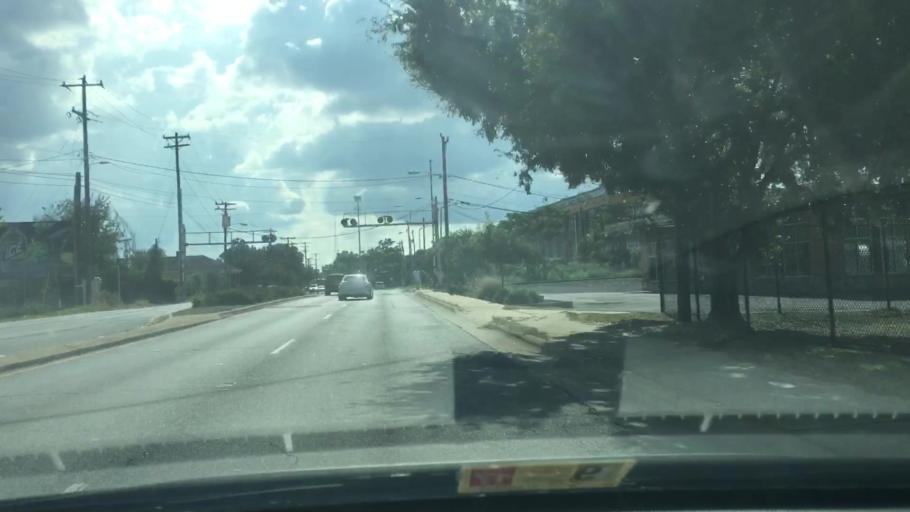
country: US
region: North Carolina
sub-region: Mecklenburg County
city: Charlotte
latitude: 35.2517
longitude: -80.8110
